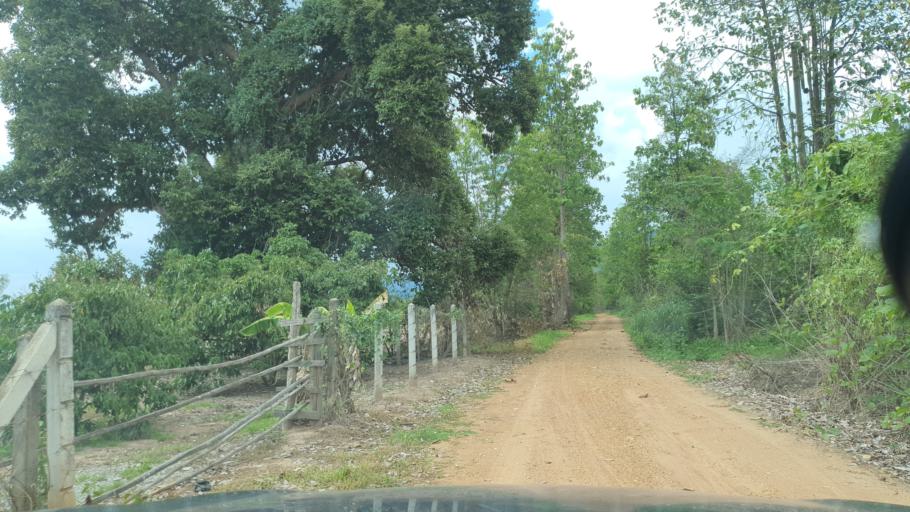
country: TH
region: Chiang Mai
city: Mae Taeng
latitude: 19.1332
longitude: 99.0338
